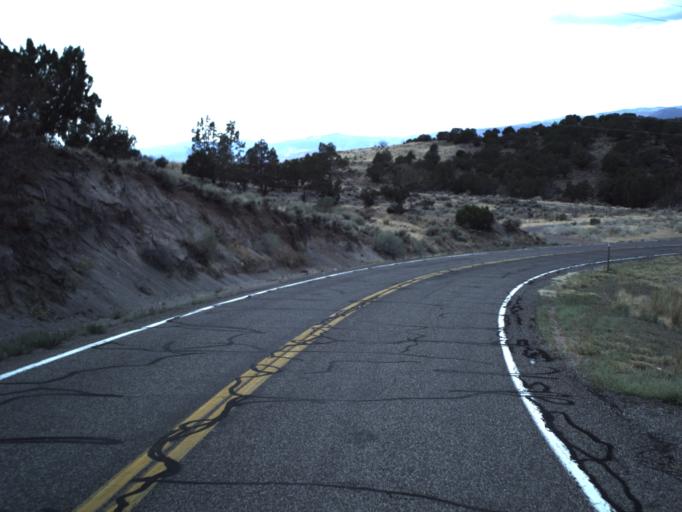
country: US
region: Utah
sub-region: Sevier County
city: Richfield
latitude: 38.7729
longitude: -111.9494
